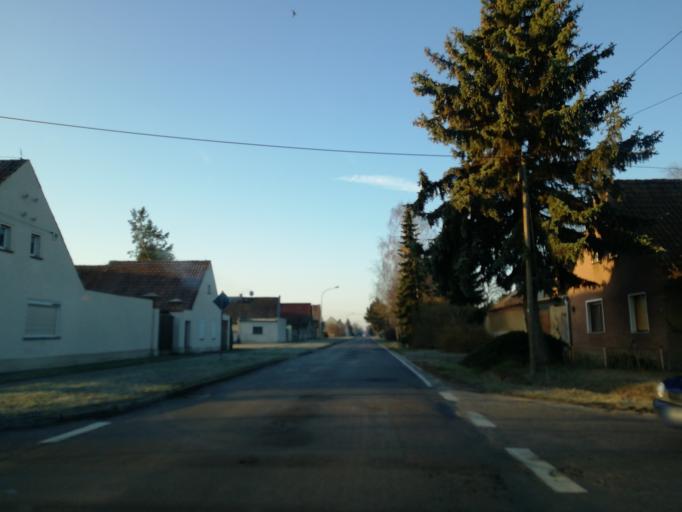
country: DE
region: Brandenburg
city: Finsterwalde
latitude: 51.6638
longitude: 13.7134
